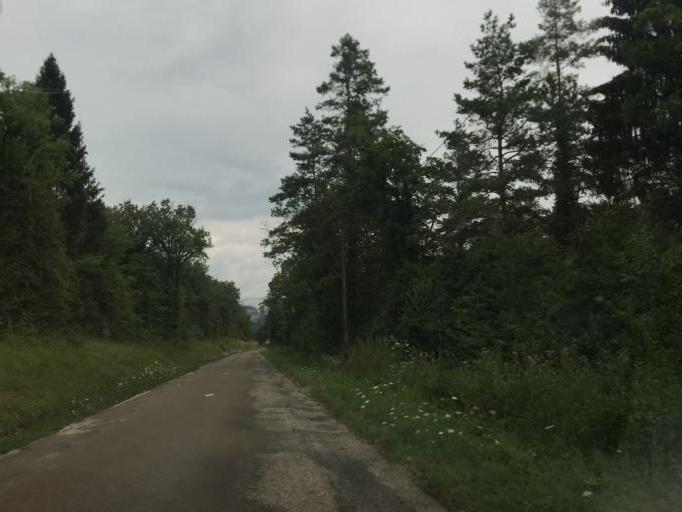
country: FR
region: Franche-Comte
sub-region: Departement du Jura
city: Lavans-les-Saint-Claude
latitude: 46.3200
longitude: 5.7553
